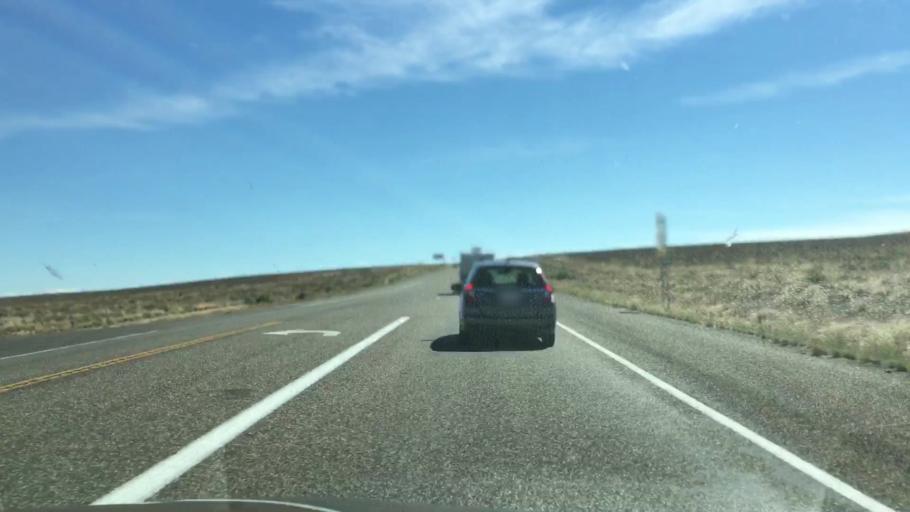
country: US
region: Arizona
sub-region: Coconino County
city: Page
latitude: 37.0062
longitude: -111.5779
